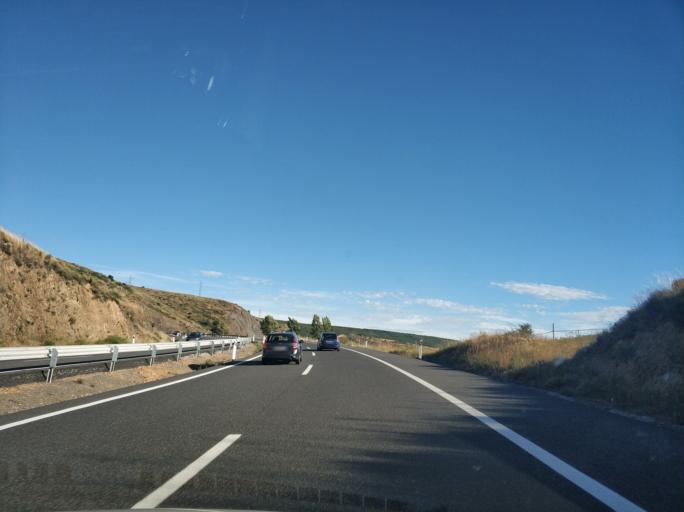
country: ES
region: Castille and Leon
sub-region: Provincia de Leon
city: Carrocera
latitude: 42.7626
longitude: -5.7764
